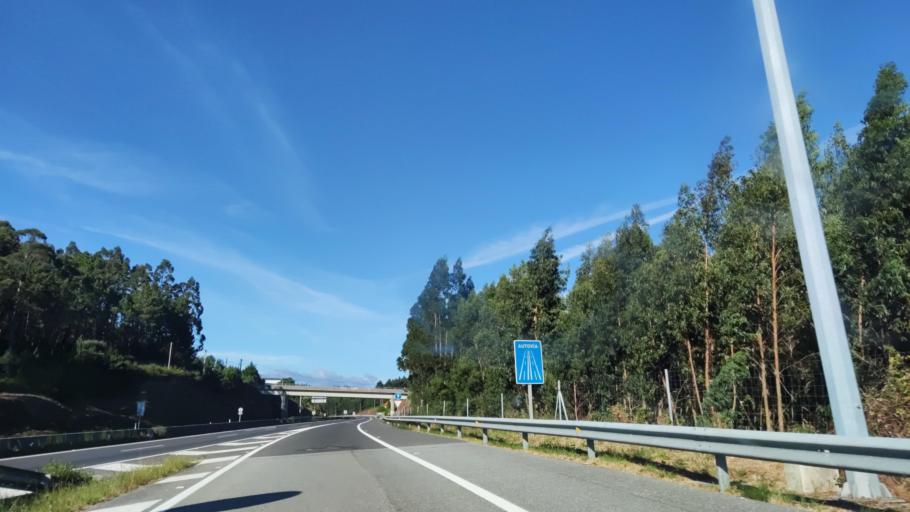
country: ES
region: Galicia
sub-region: Provincia da Coruna
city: Boiro
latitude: 42.6251
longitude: -8.9241
